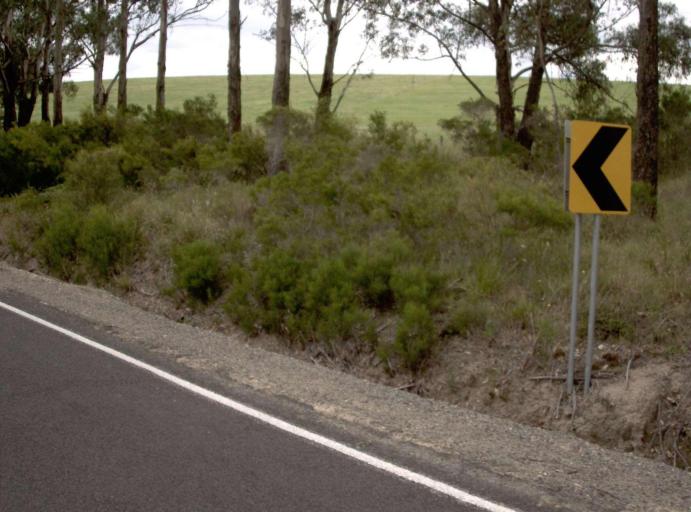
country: AU
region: New South Wales
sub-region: Bombala
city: Bombala
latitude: -37.4764
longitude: 149.1806
